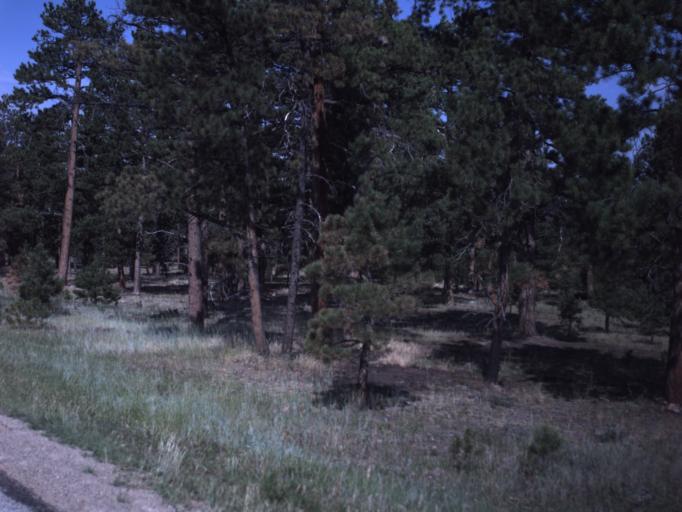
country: US
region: Utah
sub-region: Daggett County
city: Manila
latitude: 40.8579
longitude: -109.5569
